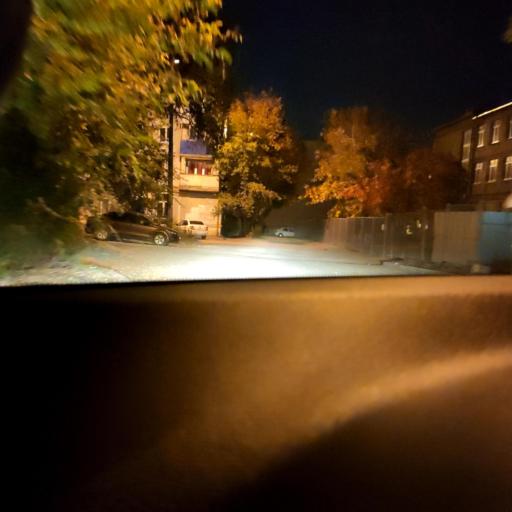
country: RU
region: Samara
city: Samara
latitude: 53.2098
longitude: 50.2284
